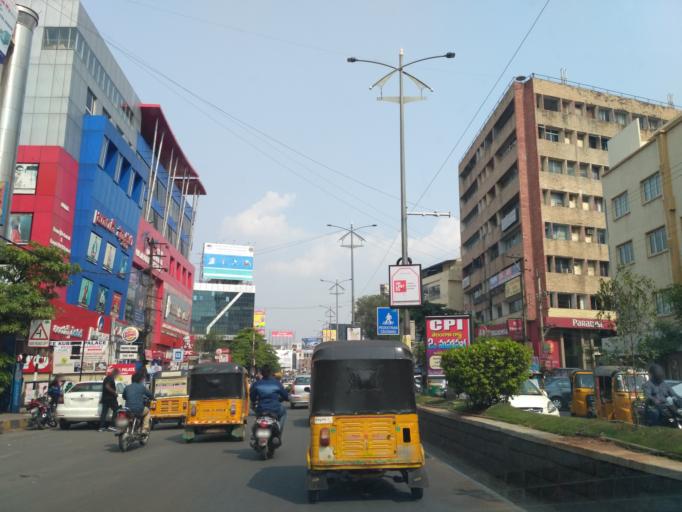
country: IN
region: Telangana
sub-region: Hyderabad
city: Hyderabad
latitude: 17.4015
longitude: 78.4854
